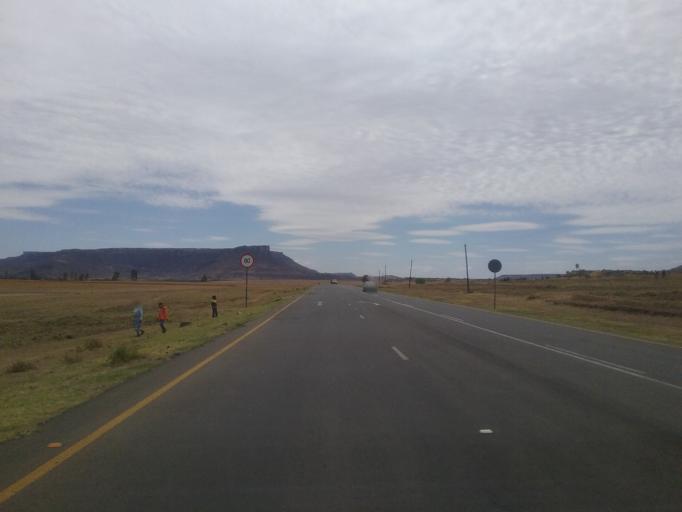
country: LS
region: Mafeteng
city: Mafeteng
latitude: -29.6819
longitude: 27.4449
